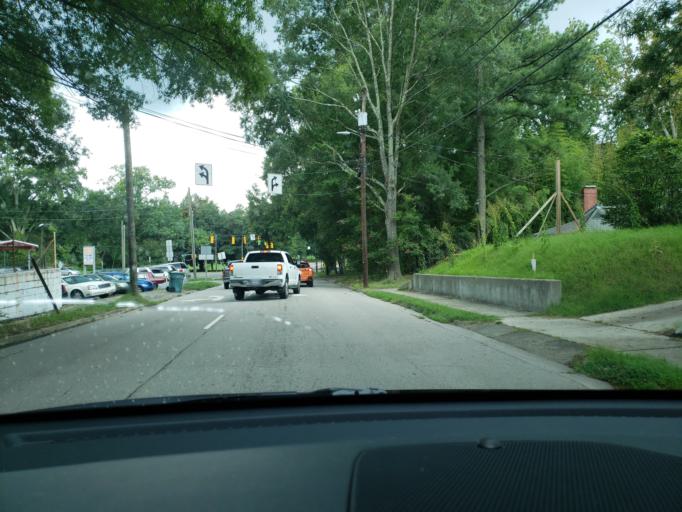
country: US
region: North Carolina
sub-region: Durham County
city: Durham
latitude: 35.9848
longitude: -78.9121
